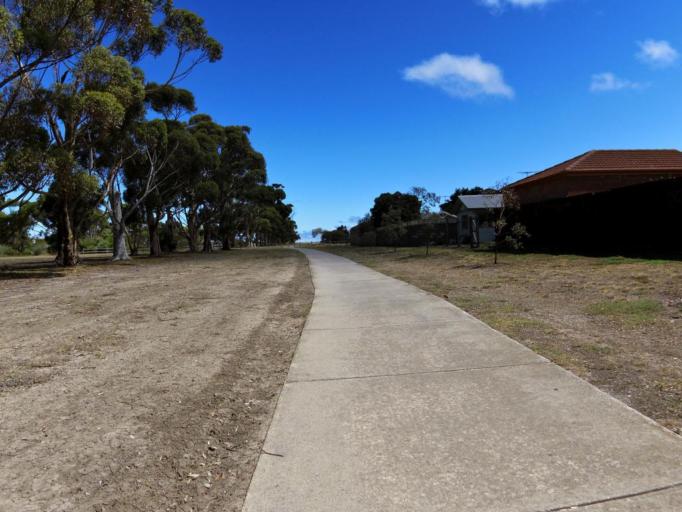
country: AU
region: Victoria
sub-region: Hobsons Bay
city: Altona Meadows
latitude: -37.8800
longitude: 144.7941
